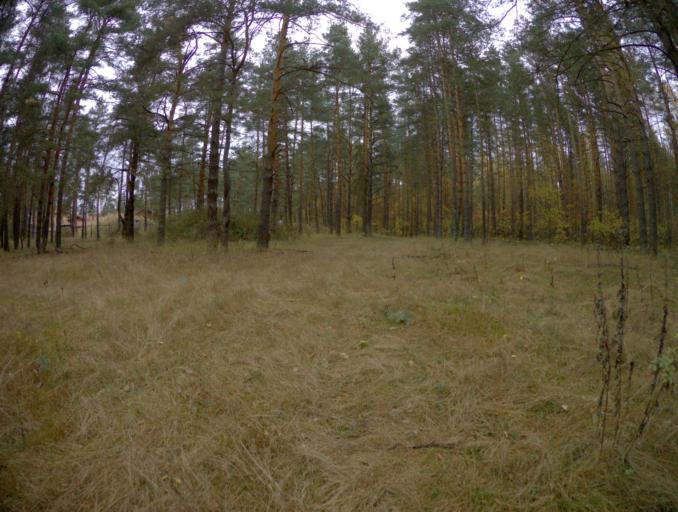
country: RU
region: Vladimir
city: Kommunar
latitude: 56.0835
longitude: 40.4402
